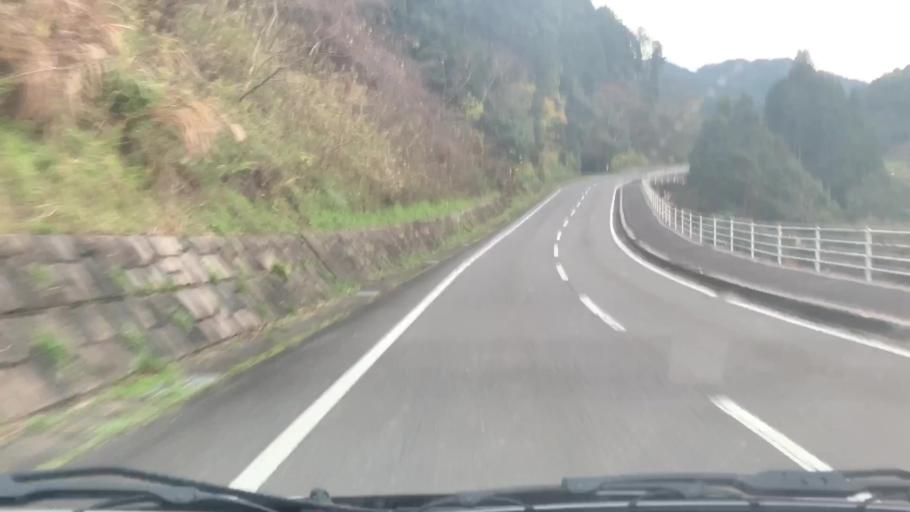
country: JP
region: Saga Prefecture
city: Kashima
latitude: 33.0230
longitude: 130.0670
